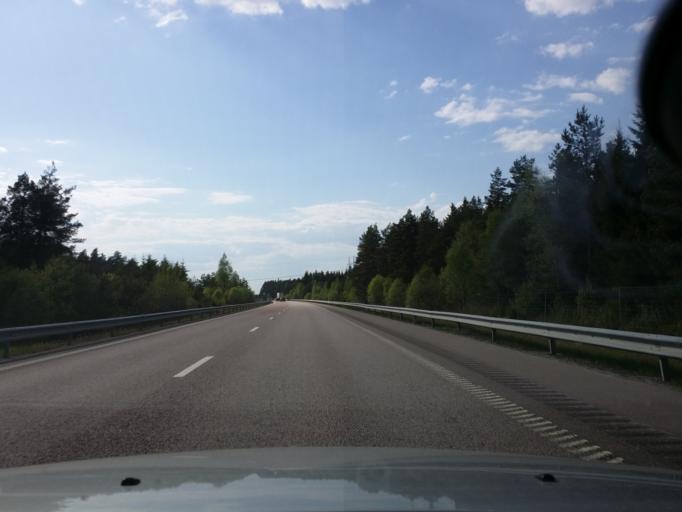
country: SE
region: Uppsala
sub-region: Enkopings Kommun
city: Grillby
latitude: 59.6439
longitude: 17.2034
